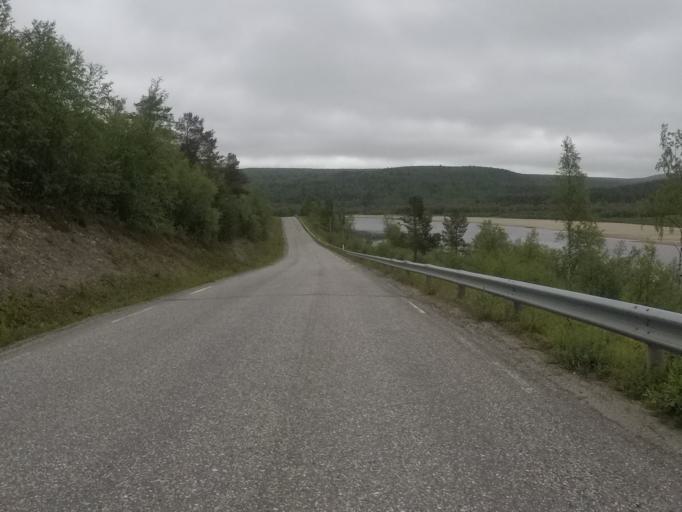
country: NO
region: Finnmark Fylke
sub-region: Karasjok
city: Karasjohka
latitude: 69.5161
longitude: 25.8629
